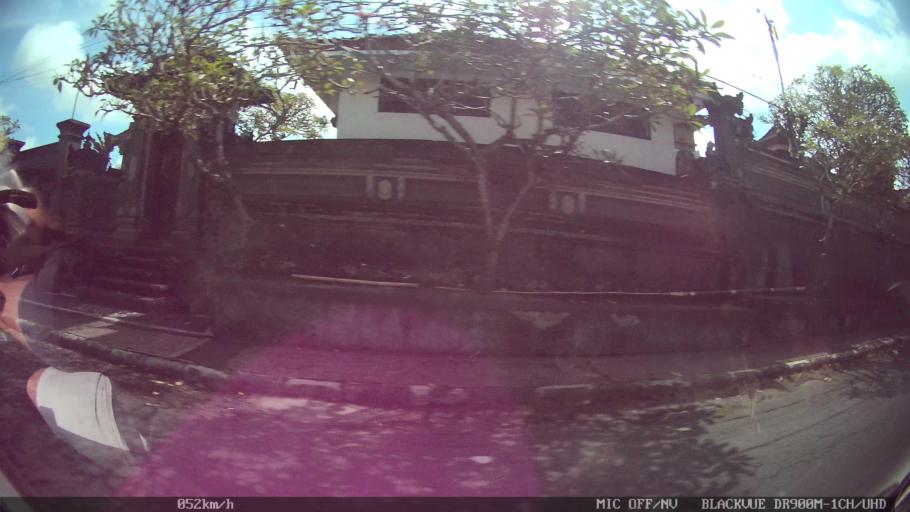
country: ID
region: Bali
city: Banjar Kelodan
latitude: -8.5293
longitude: 115.3287
